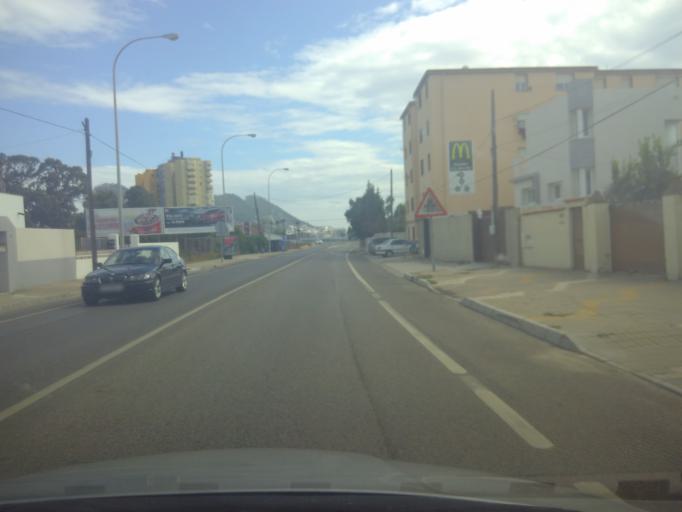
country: ES
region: Andalusia
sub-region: Provincia de Cadiz
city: La Linea de la Concepcion
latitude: 36.1716
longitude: -5.3714
